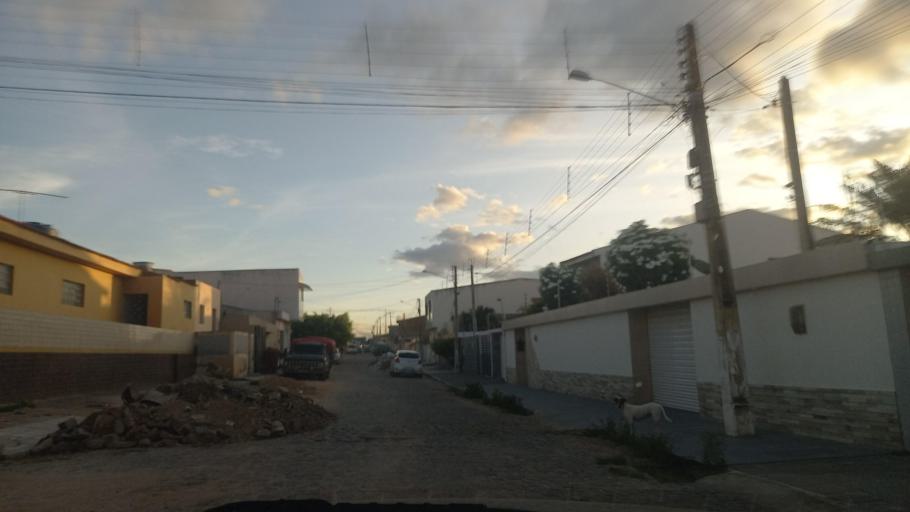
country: BR
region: Pernambuco
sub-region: Bezerros
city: Bezerros
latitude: -8.2386
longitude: -35.7486
